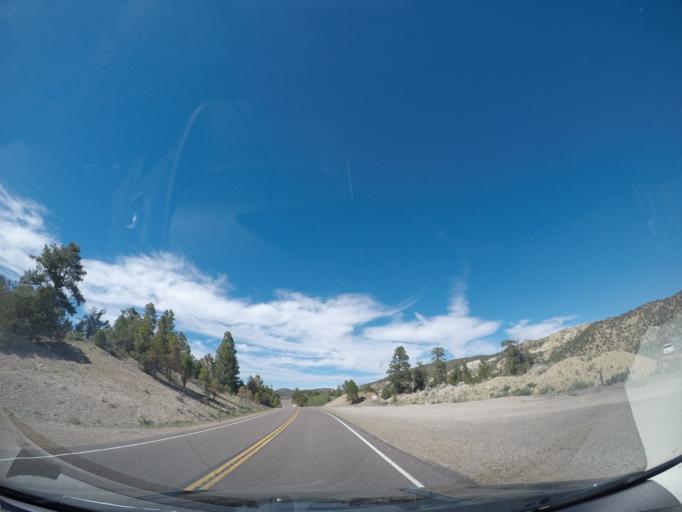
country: US
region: Utah
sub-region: Garfield County
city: Panguitch
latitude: 37.6982
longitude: -111.7916
